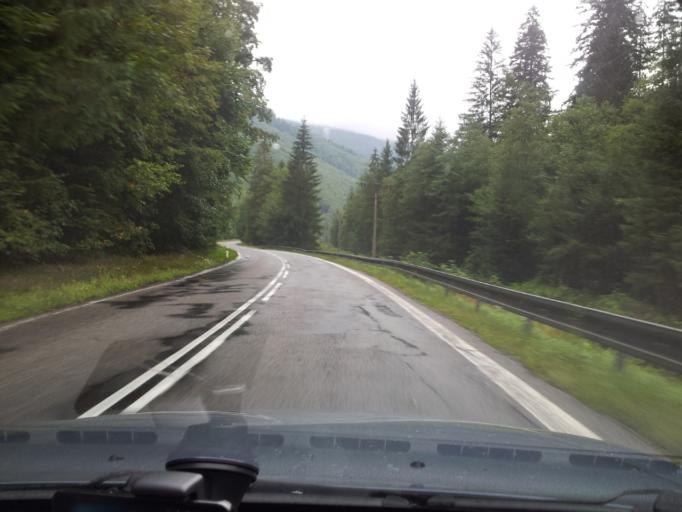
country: SK
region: Banskobystricky
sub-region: Okres Banska Bystrica
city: Brezno
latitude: 48.8709
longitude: 19.6531
